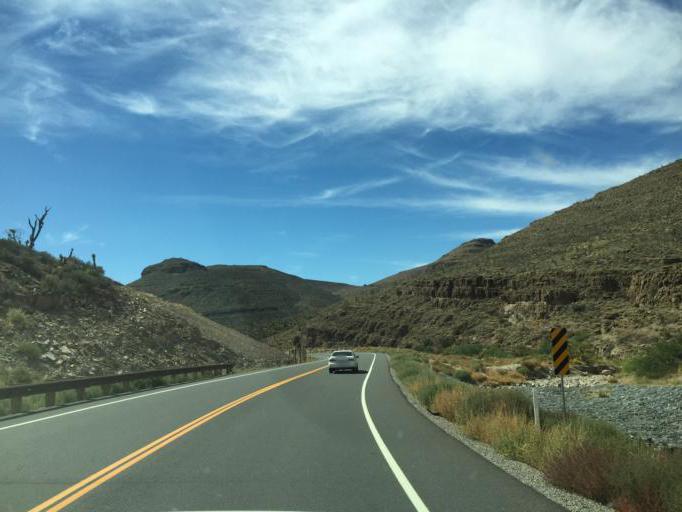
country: US
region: Arizona
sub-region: Mohave County
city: Meadview
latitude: 35.9005
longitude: -113.9399
